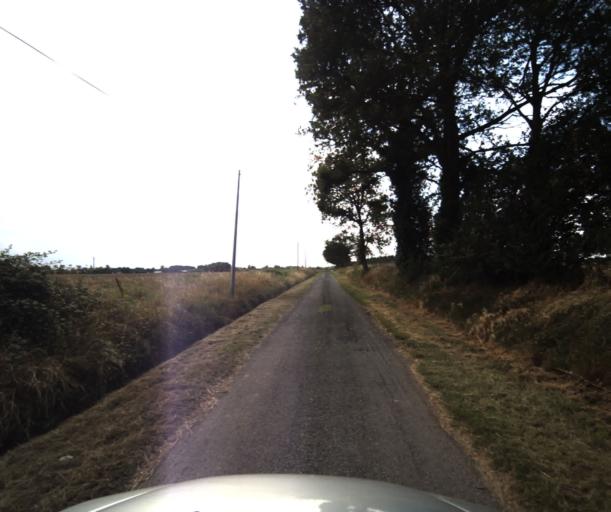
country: FR
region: Midi-Pyrenees
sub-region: Departement de la Haute-Garonne
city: Eaunes
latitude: 43.4312
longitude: 1.3178
